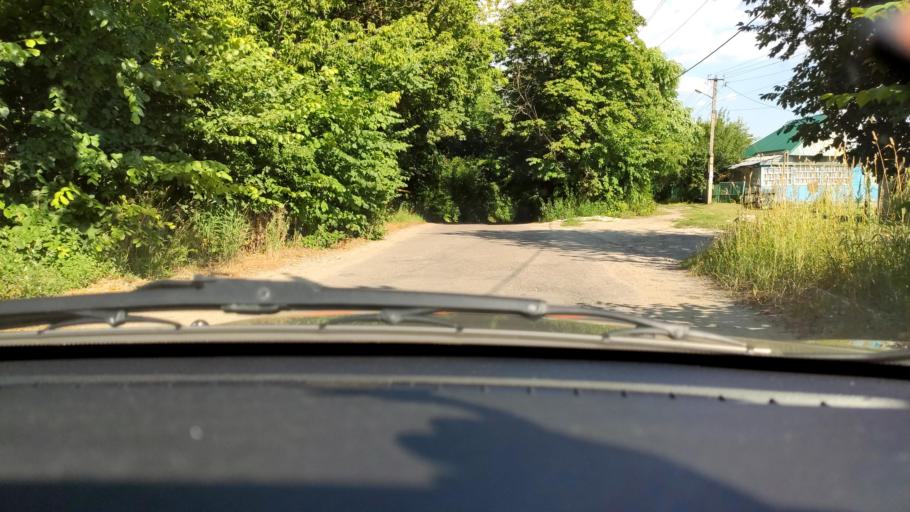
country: RU
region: Voronezj
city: Ramon'
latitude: 51.8246
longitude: 39.2718
